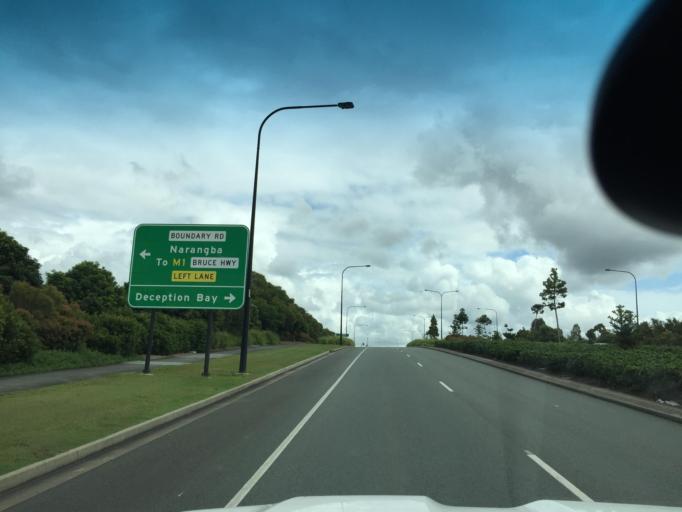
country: AU
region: Queensland
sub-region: Moreton Bay
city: Deception Bay
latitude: -27.2113
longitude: 152.9987
